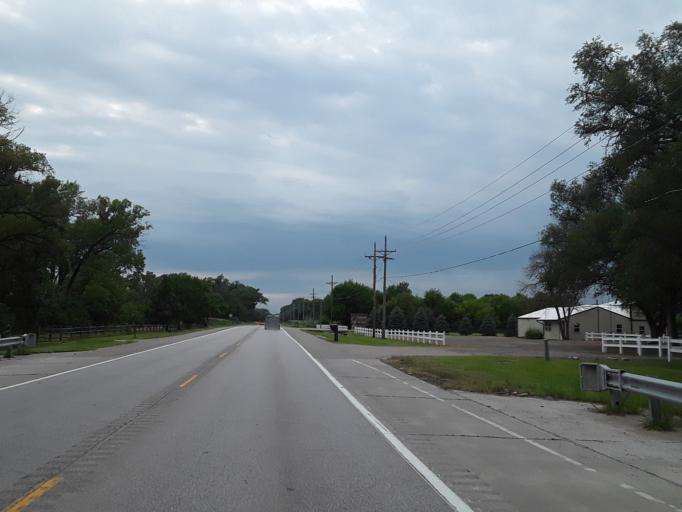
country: US
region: Nebraska
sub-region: Saunders County
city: Yutan
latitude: 41.2338
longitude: -96.3371
